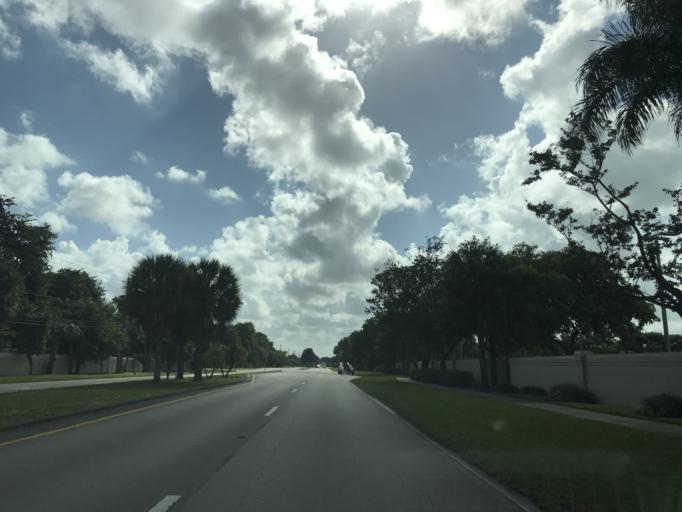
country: US
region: Florida
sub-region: Broward County
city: Coconut Creek
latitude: 26.2723
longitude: -80.1947
